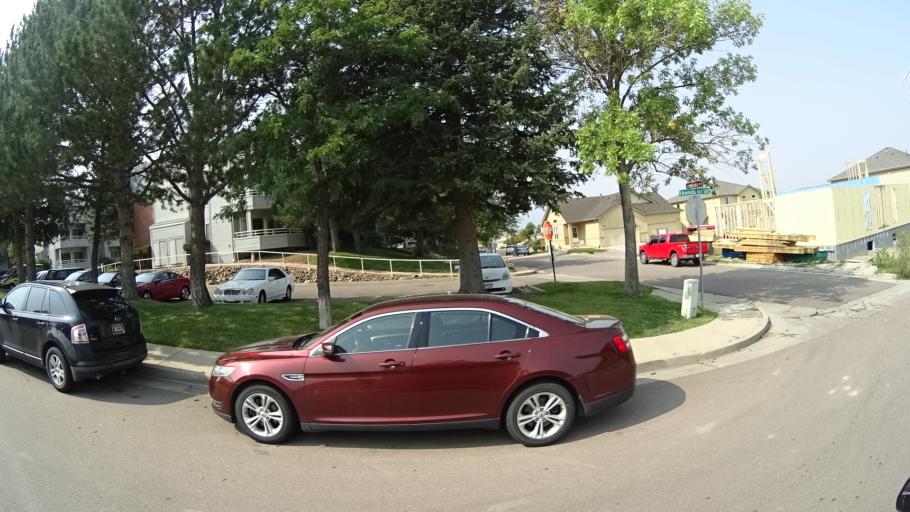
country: US
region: Colorado
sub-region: El Paso County
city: Stratmoor
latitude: 38.8190
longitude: -104.7594
